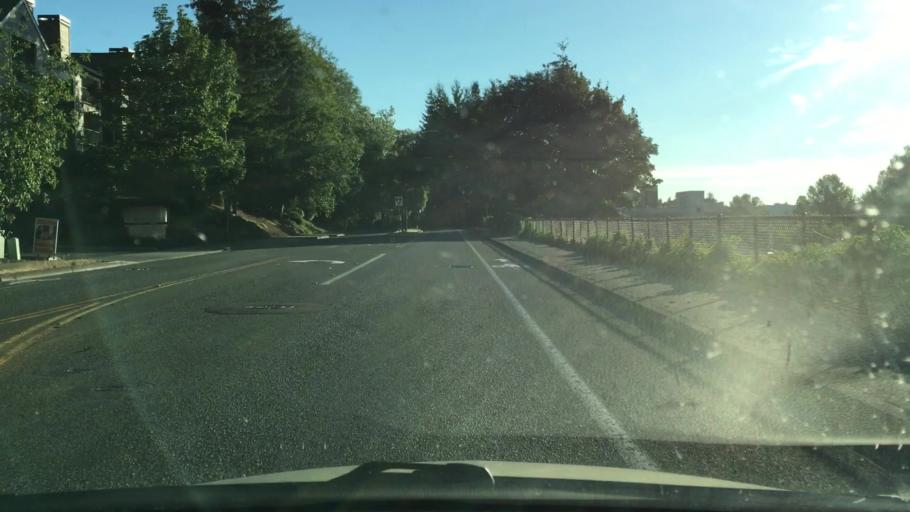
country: US
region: Washington
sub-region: King County
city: Kingsgate
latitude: 47.7100
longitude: -122.1690
